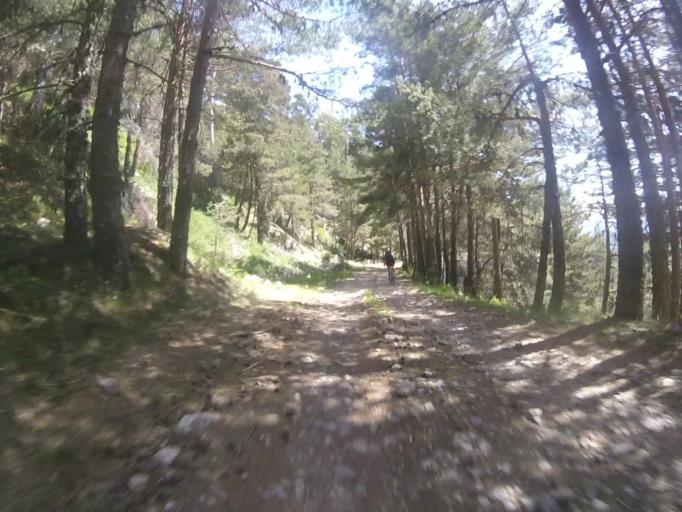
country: ES
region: Madrid
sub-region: Provincia de Madrid
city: Cercedilla
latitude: 40.7984
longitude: -4.0615
